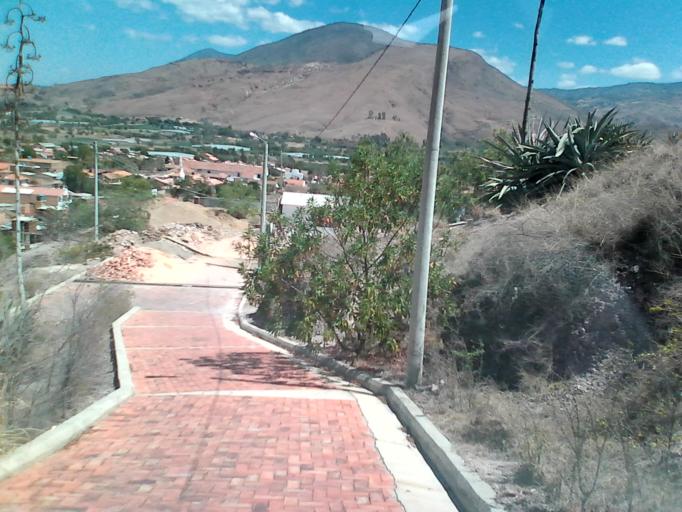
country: CO
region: Boyaca
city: Sachica
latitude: 5.5803
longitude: -73.5442
